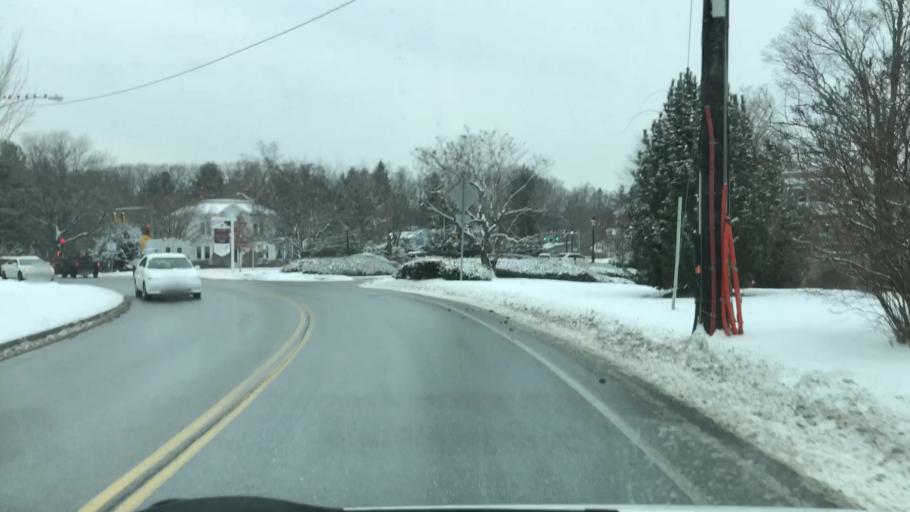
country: US
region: Massachusetts
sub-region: Berkshire County
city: Dalton
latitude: 42.4703
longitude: -73.1790
